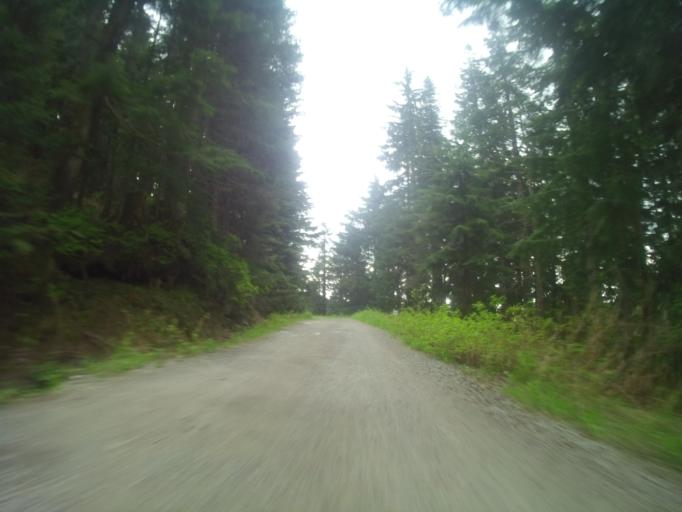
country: CA
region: British Columbia
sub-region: Fraser Valley Regional District
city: North Vancouver
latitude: 49.3820
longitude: -123.0661
